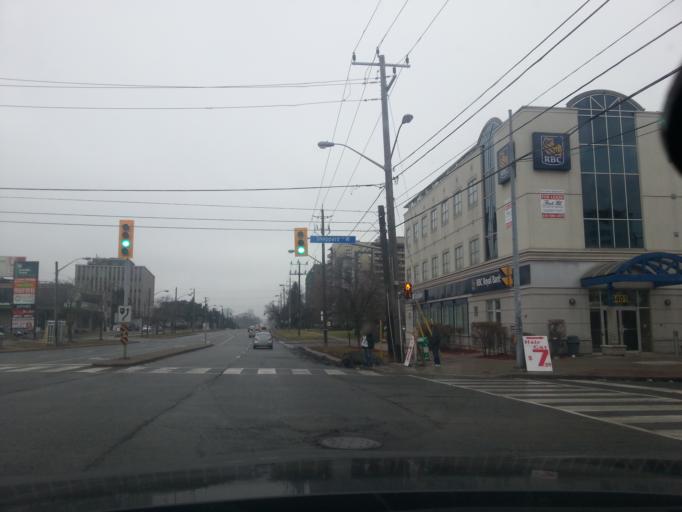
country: CA
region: Ontario
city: North York
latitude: 43.7554
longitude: -79.4383
